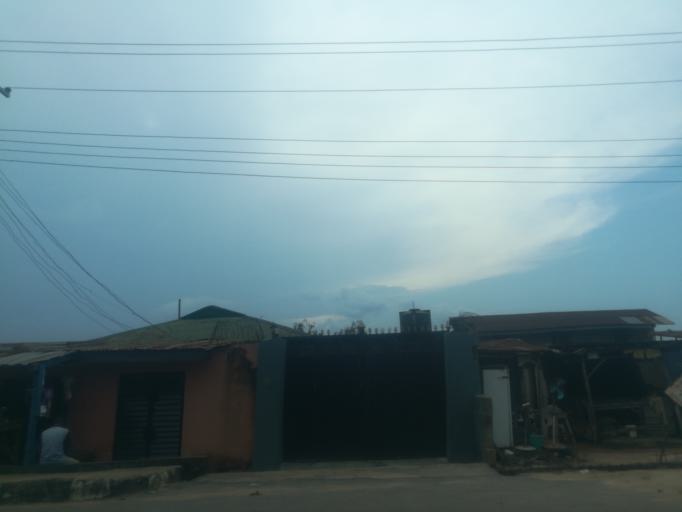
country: NG
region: Oyo
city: Ibadan
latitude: 7.3809
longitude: 3.8288
